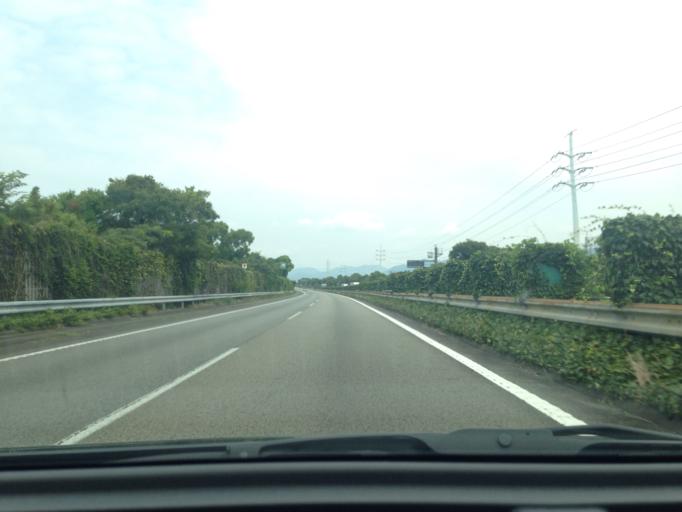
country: JP
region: Shizuoka
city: Fujieda
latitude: 34.8438
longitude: 138.2821
